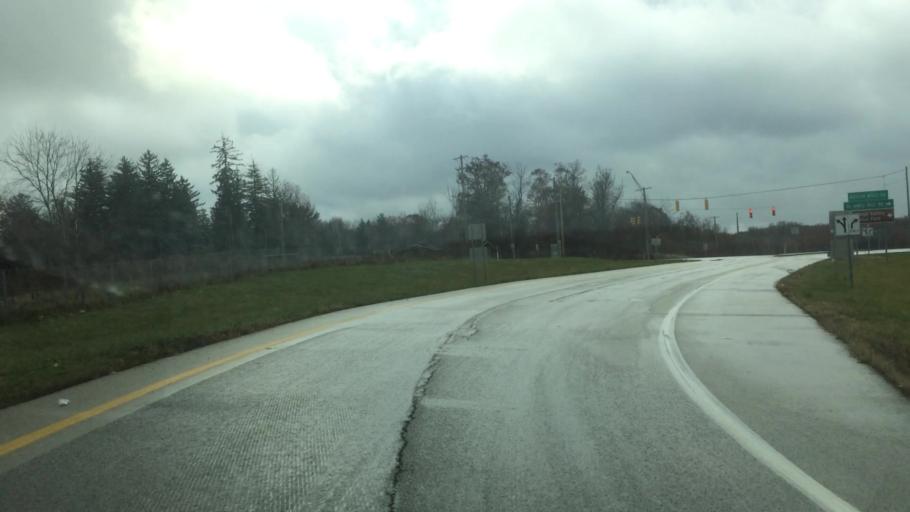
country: US
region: Ohio
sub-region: Summit County
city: Boston Heights
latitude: 41.2551
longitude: -81.4977
